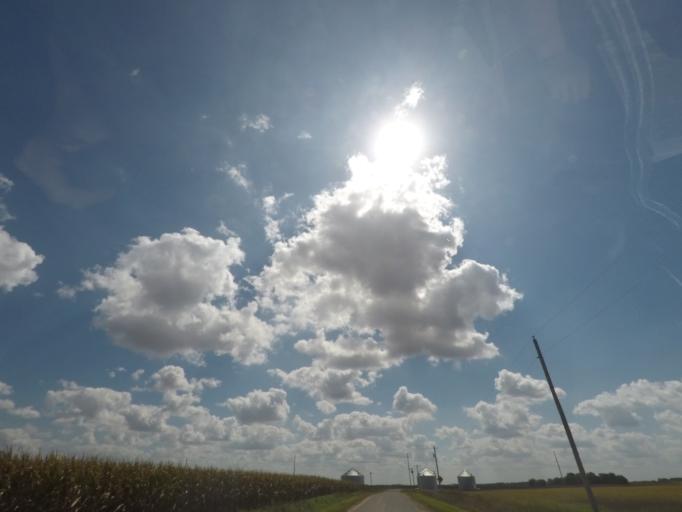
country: US
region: Iowa
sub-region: Story County
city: Nevada
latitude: 42.0363
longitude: -93.3621
